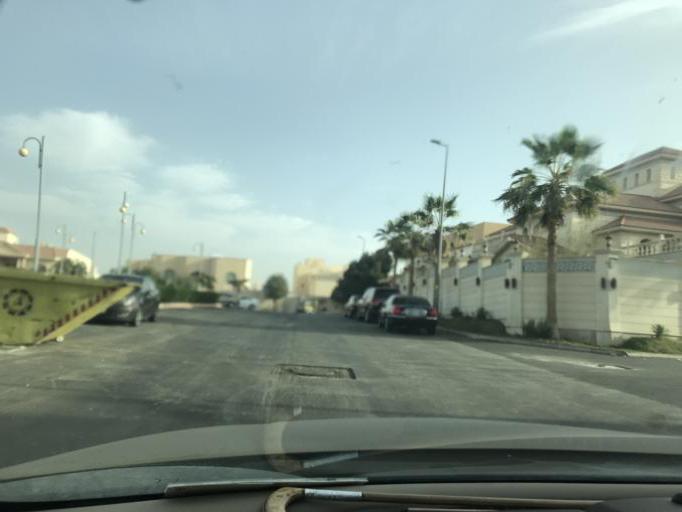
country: SA
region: Ar Riyad
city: Riyadh
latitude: 24.7386
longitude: 46.7516
